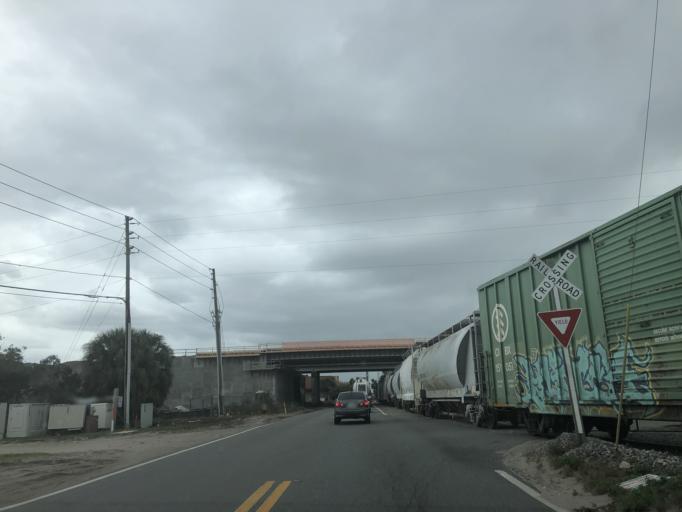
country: US
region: Florida
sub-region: Orange County
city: Southchase
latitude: 28.4067
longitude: -81.3927
